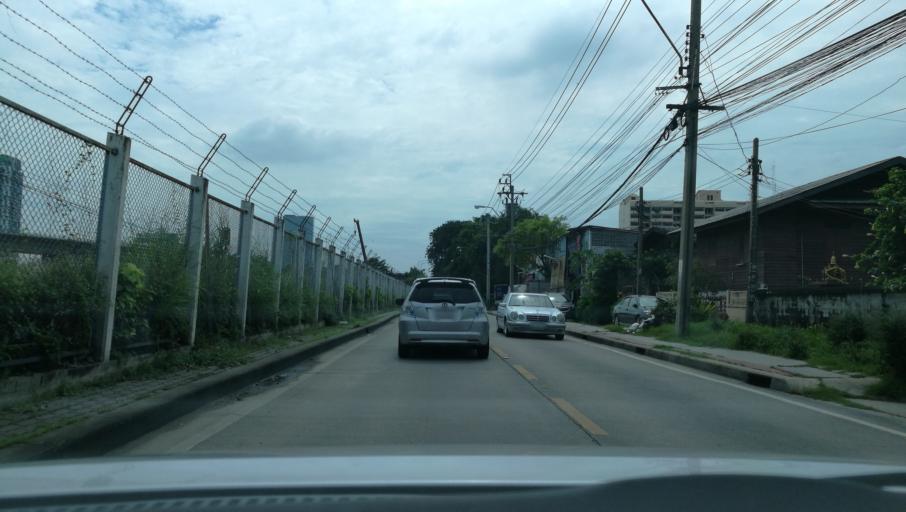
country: TH
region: Bangkok
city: Bang Sue
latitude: 13.7996
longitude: 100.5380
